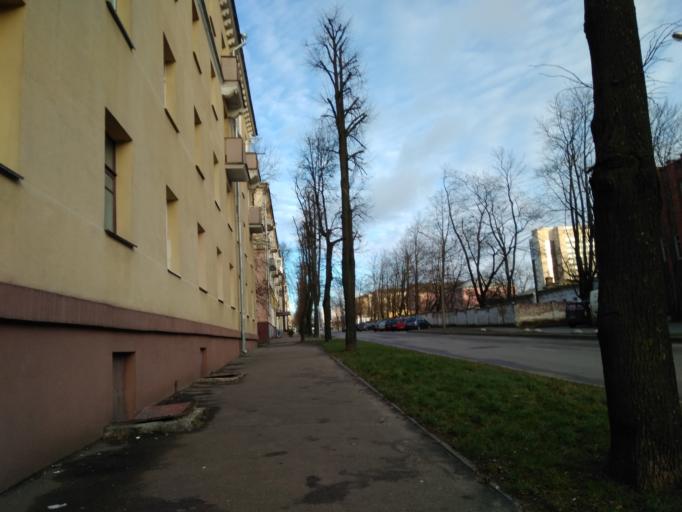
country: BY
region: Minsk
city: Minsk
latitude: 53.8978
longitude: 27.6012
